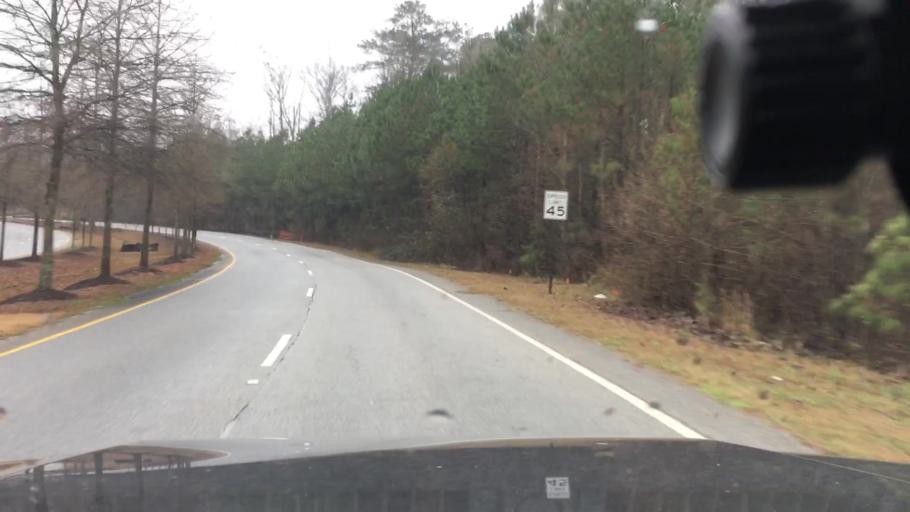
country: US
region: Georgia
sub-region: Coweta County
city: East Newnan
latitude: 33.3860
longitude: -84.7521
